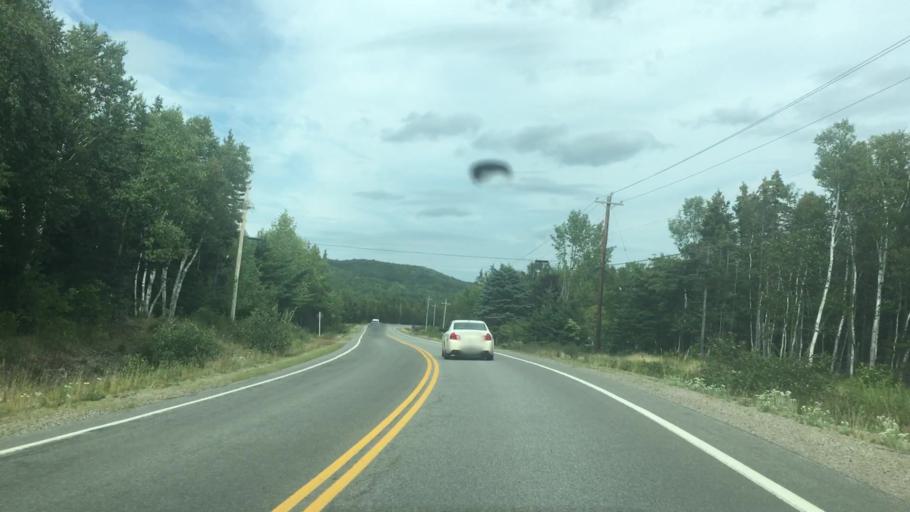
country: CA
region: Nova Scotia
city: Sydney Mines
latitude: 46.5087
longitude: -60.4314
